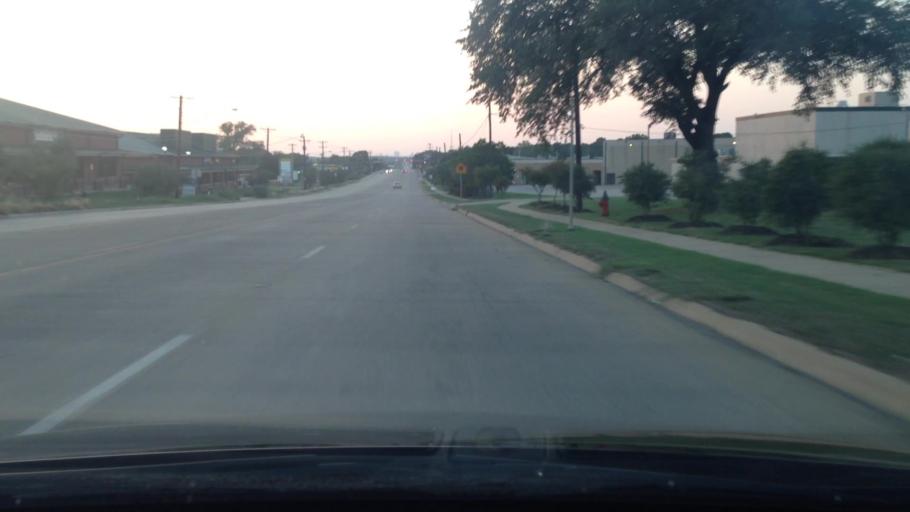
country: US
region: Texas
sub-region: Tarrant County
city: Kennedale
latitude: 32.6475
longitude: -97.2222
